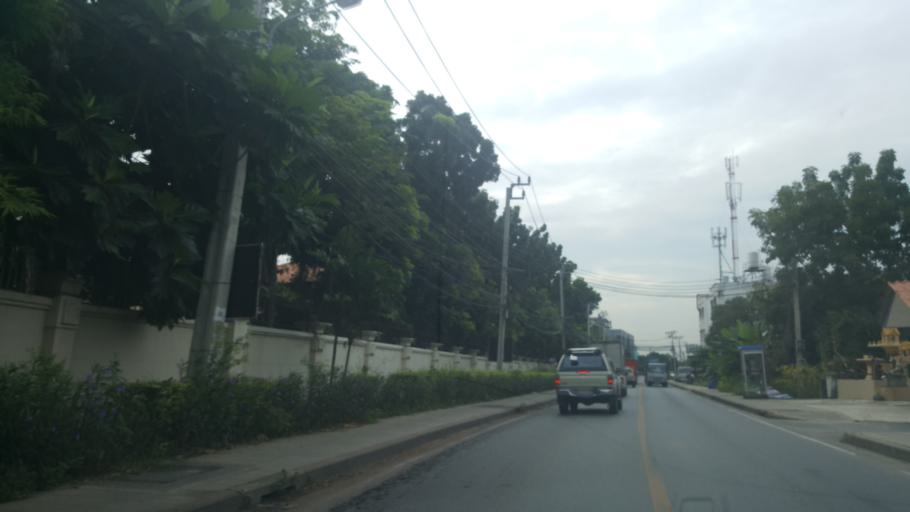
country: TH
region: Bangkok
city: Bang Bon
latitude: 13.6753
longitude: 100.4016
